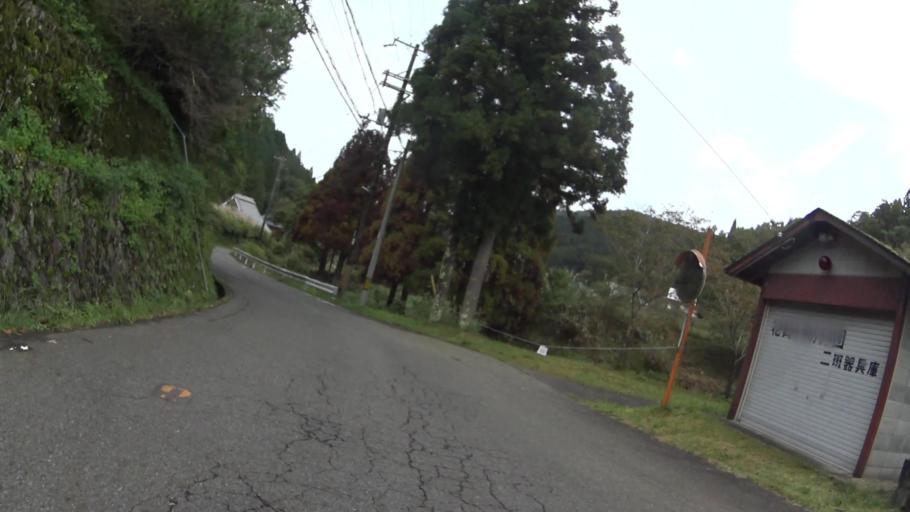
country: JP
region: Shiga Prefecture
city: Kitahama
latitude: 35.1735
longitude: 135.7833
